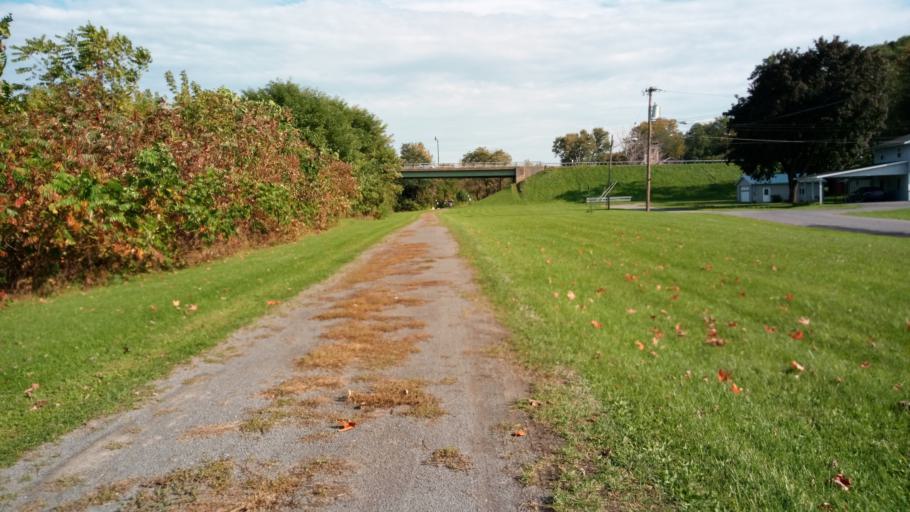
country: US
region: New York
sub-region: Wayne County
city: Clyde
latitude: 43.0813
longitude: -76.8742
